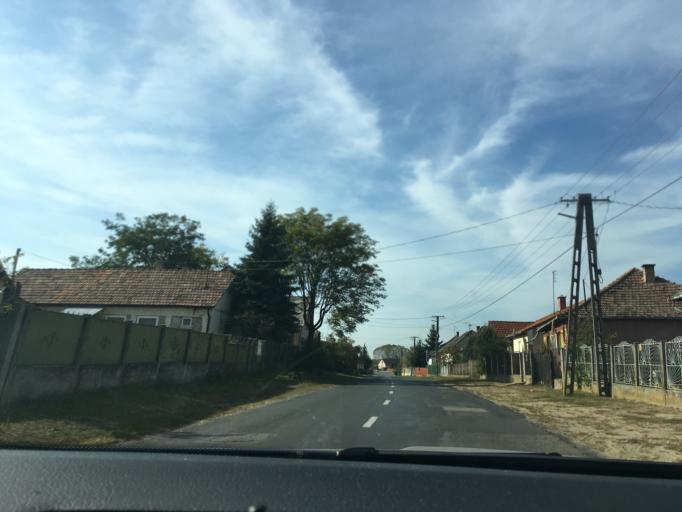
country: HU
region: Hajdu-Bihar
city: Nyirabrany
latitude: 47.5317
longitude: 21.9958
